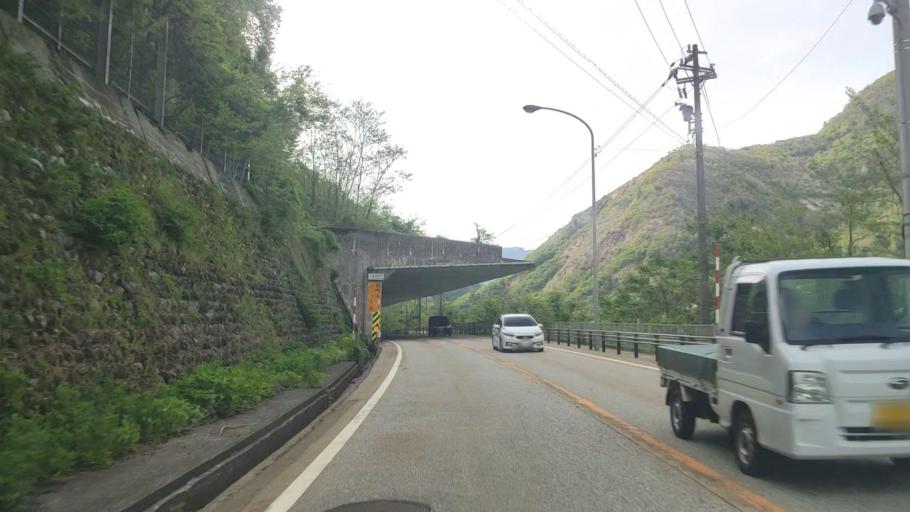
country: JP
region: Gifu
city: Takayama
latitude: 36.3472
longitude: 137.2937
